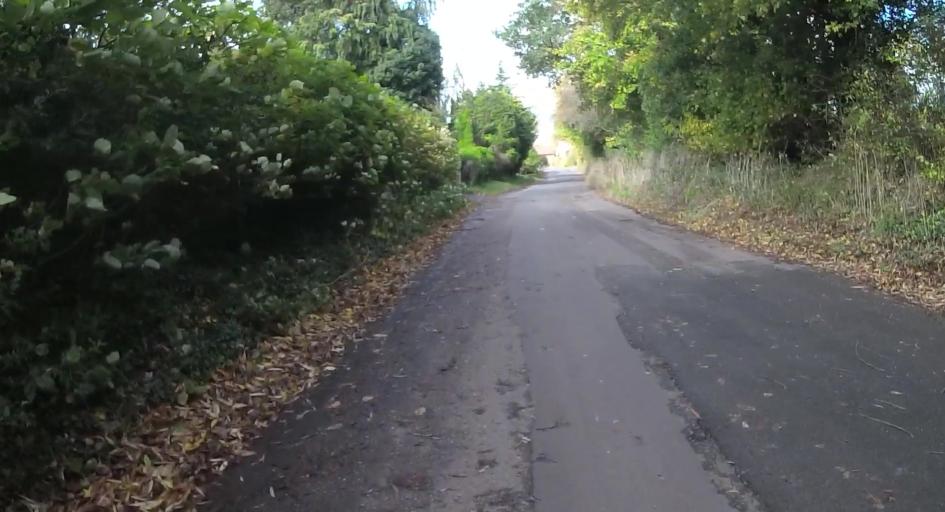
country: GB
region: England
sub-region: Hampshire
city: Old Basing
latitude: 51.2809
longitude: -1.0485
